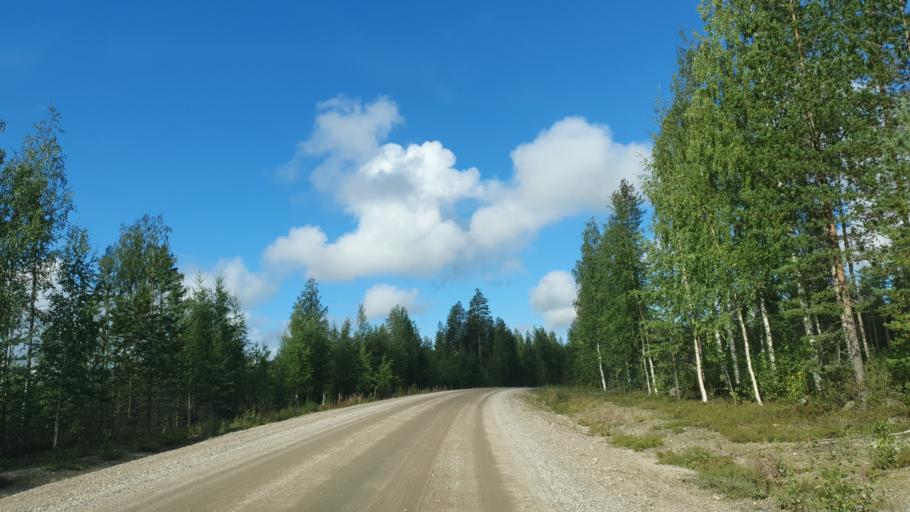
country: FI
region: Kainuu
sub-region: Kehys-Kainuu
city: Kuhmo
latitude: 63.9845
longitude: 29.2291
